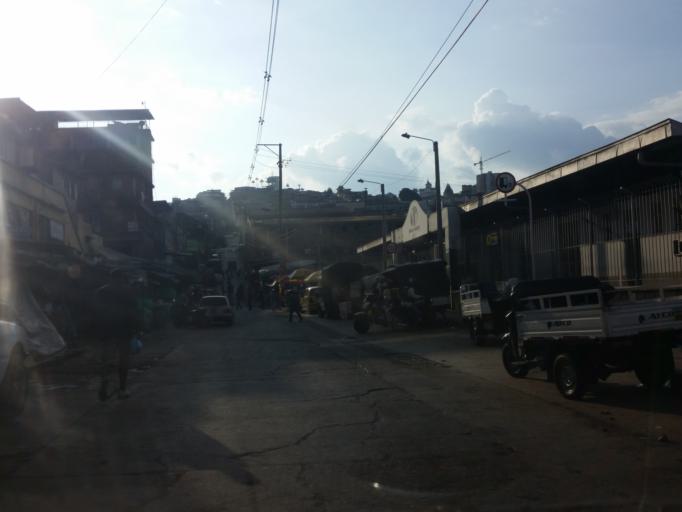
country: CO
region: Caldas
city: Manizales
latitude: 5.0724
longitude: -75.5167
